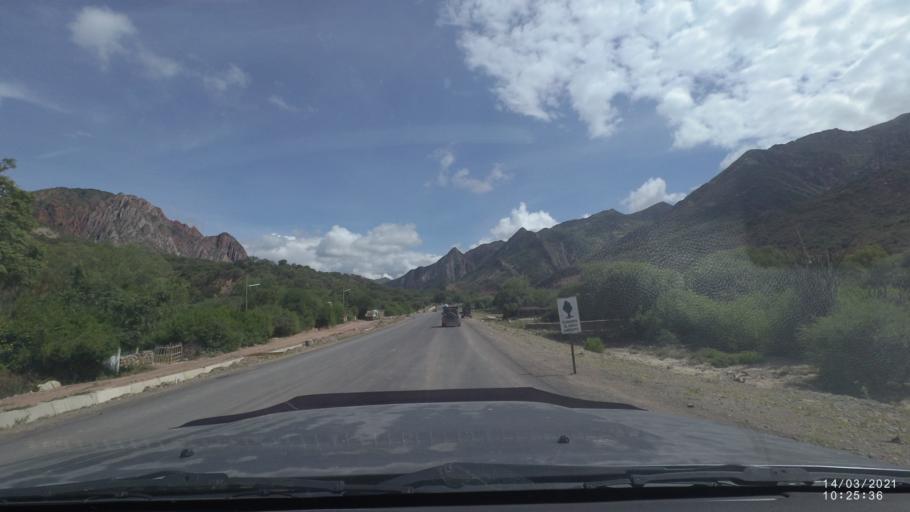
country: BO
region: Cochabamba
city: Cliza
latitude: -17.9086
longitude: -65.8797
